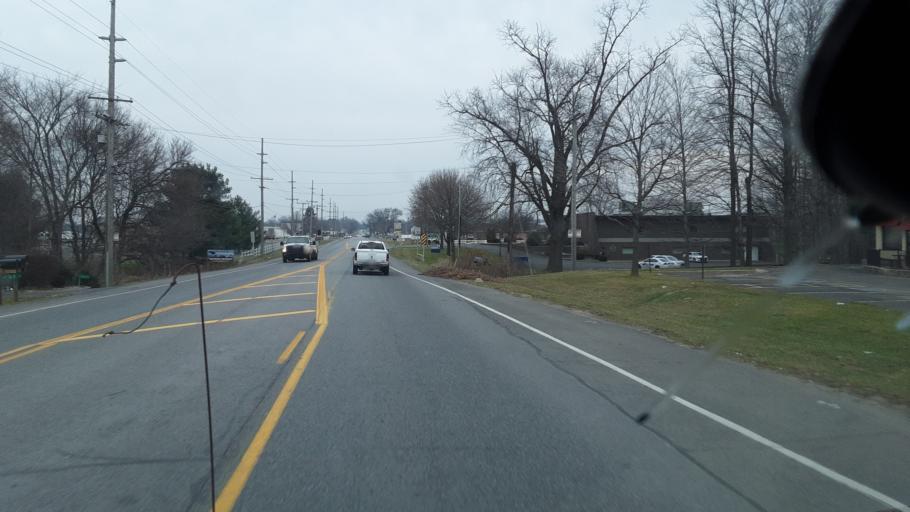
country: US
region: Indiana
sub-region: Elkhart County
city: Middlebury
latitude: 41.6837
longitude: -85.7018
